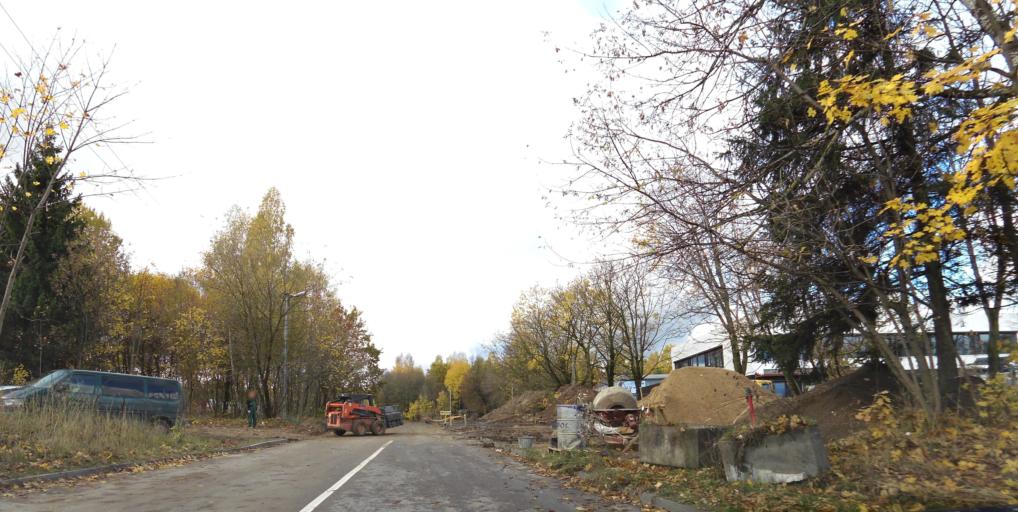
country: LT
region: Vilnius County
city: Vilkpede
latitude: 54.6462
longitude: 25.2652
